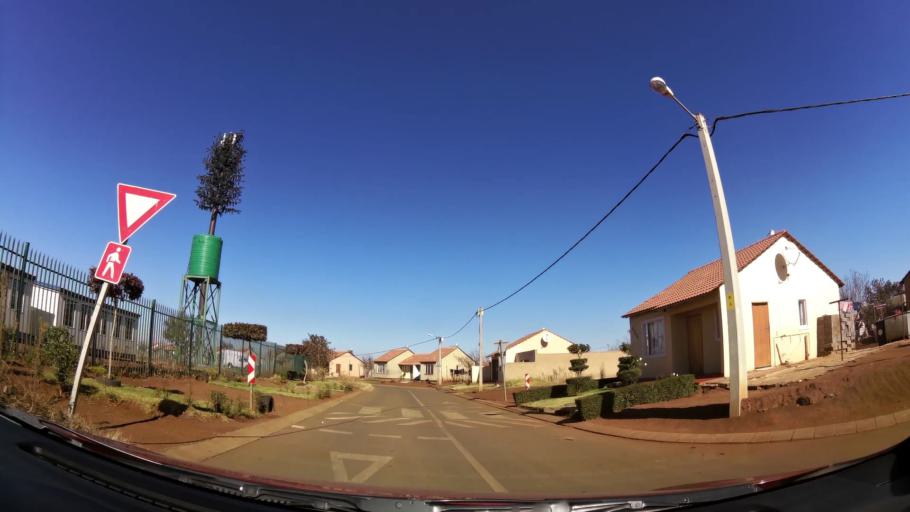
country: ZA
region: Gauteng
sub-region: City of Johannesburg Metropolitan Municipality
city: Soweto
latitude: -26.2393
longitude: 27.8004
